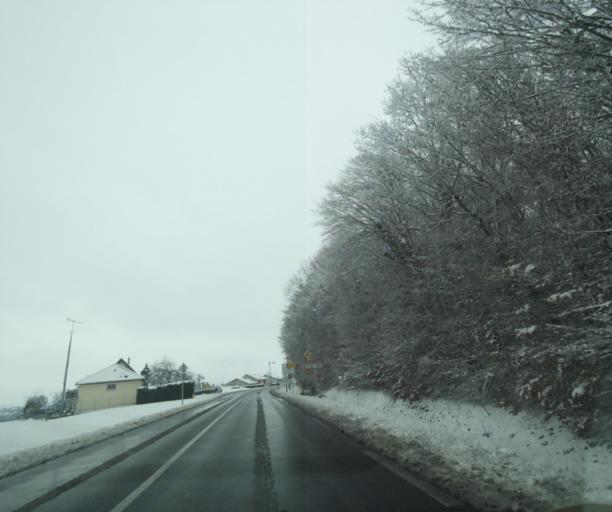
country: FR
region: Champagne-Ardenne
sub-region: Departement de la Haute-Marne
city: Montier-en-Der
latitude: 48.4857
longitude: 4.7746
